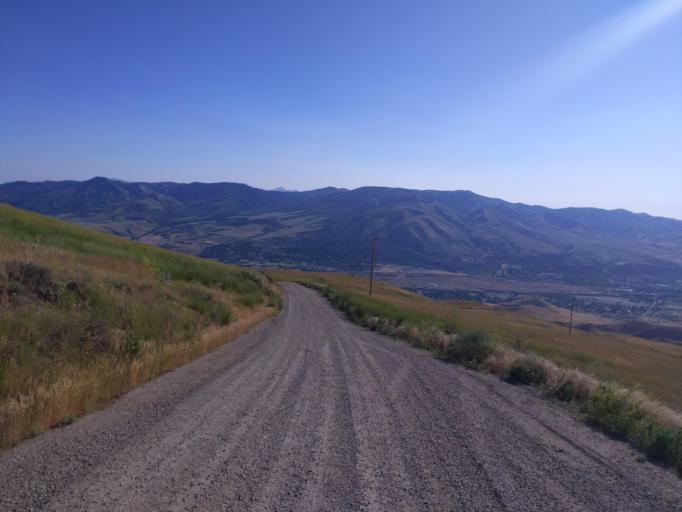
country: US
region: Idaho
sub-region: Bannock County
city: Pocatello
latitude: 42.8499
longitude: -112.3656
